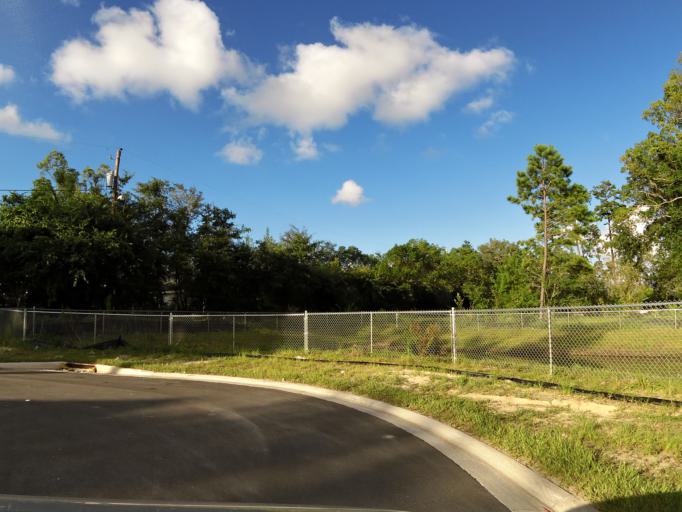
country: US
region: Florida
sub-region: Duval County
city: Jacksonville
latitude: 30.4232
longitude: -81.6950
